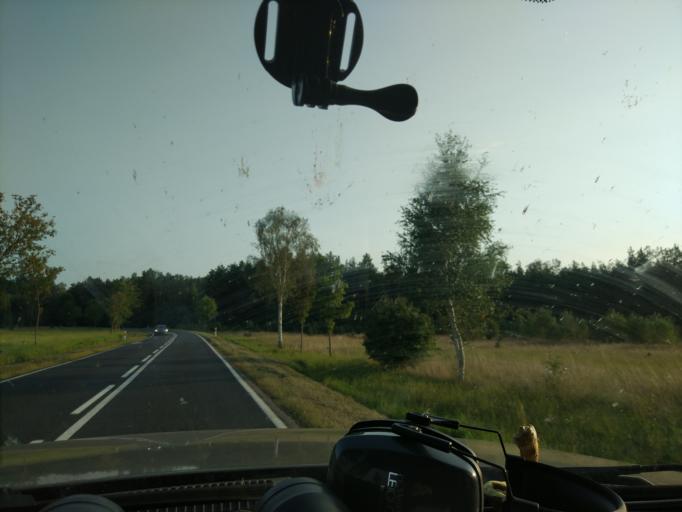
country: PL
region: Warmian-Masurian Voivodeship
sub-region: Powiat szczycienski
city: Wielbark
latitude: 53.3465
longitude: 20.8999
